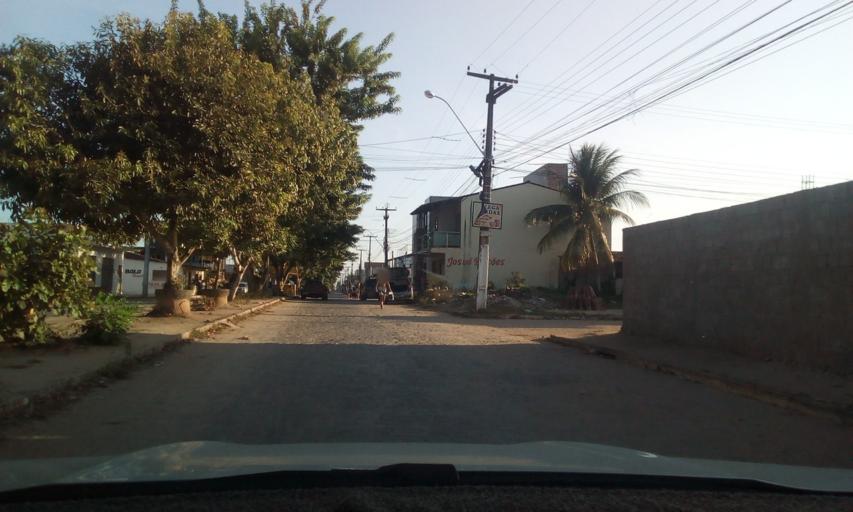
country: BR
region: Paraiba
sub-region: Bayeux
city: Bayeux
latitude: -7.1773
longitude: -34.9327
